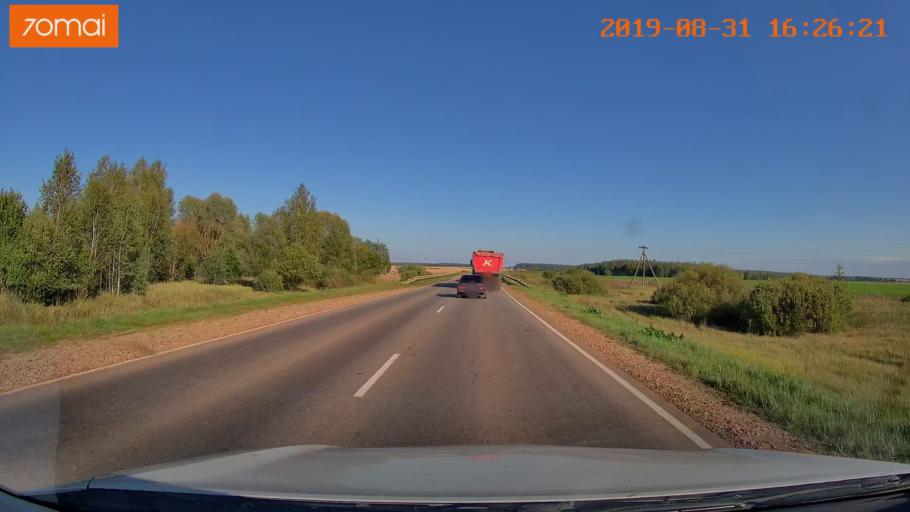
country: RU
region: Kaluga
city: Babynino
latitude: 54.5184
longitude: 35.7331
